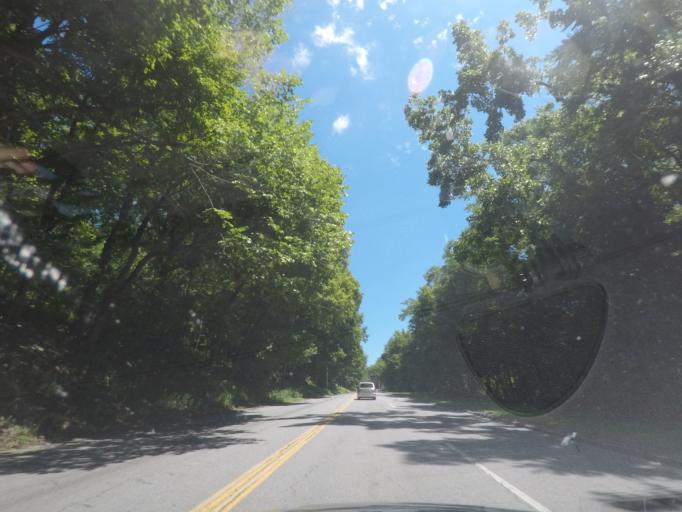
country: US
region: New York
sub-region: Rensselaer County
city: Troy
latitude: 42.7045
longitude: -73.6946
